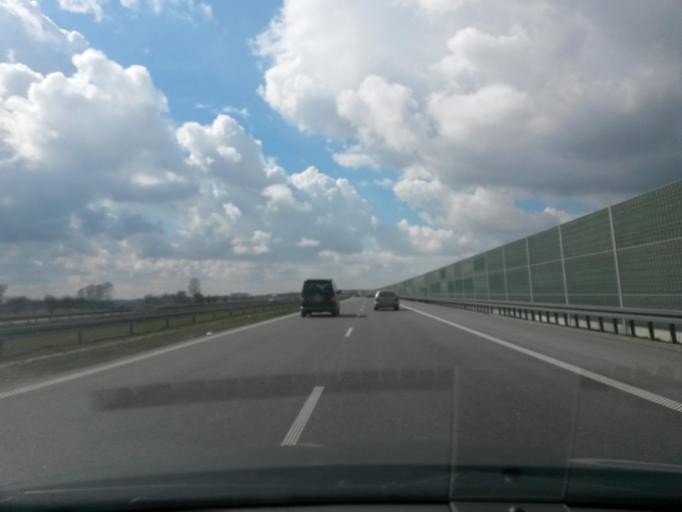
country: PL
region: Masovian Voivodeship
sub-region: Powiat warszawski zachodni
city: Bieniewice
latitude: 52.1312
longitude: 20.5476
